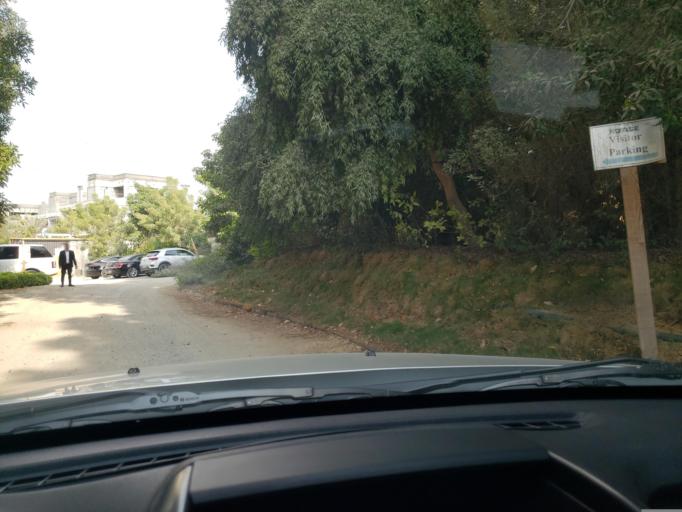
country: AE
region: Dubai
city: Dubai
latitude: 25.0991
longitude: 55.3182
